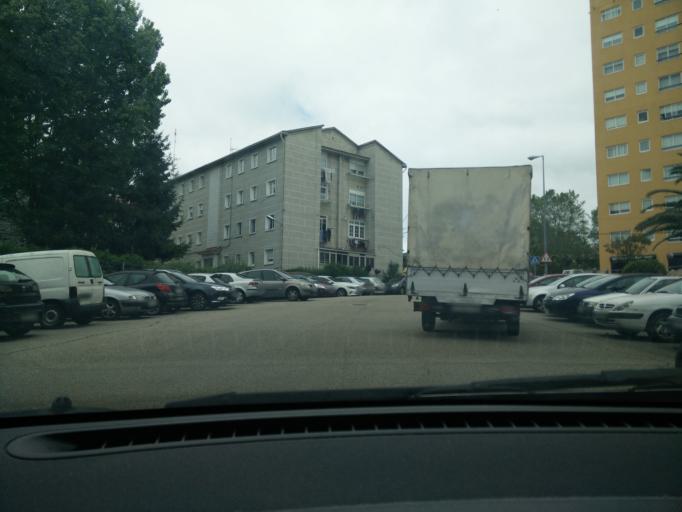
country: ES
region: Galicia
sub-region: Provincia de Pontevedra
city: Vigo
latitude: 42.2124
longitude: -8.7425
